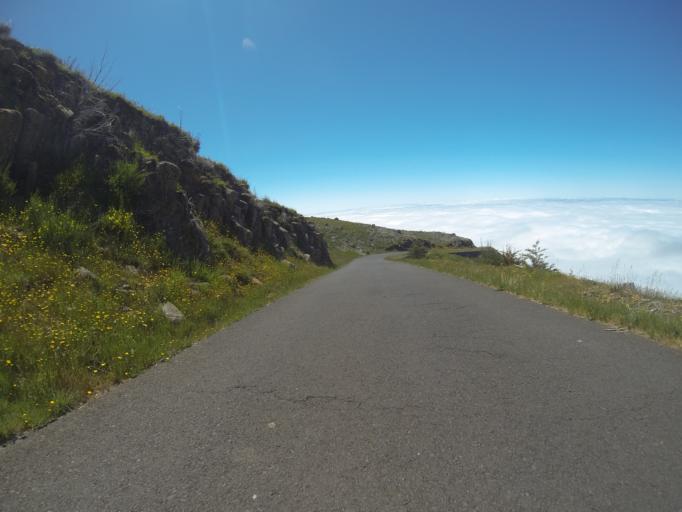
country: PT
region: Madeira
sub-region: Funchal
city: Nossa Senhora do Monte
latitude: 32.7064
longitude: -16.9148
